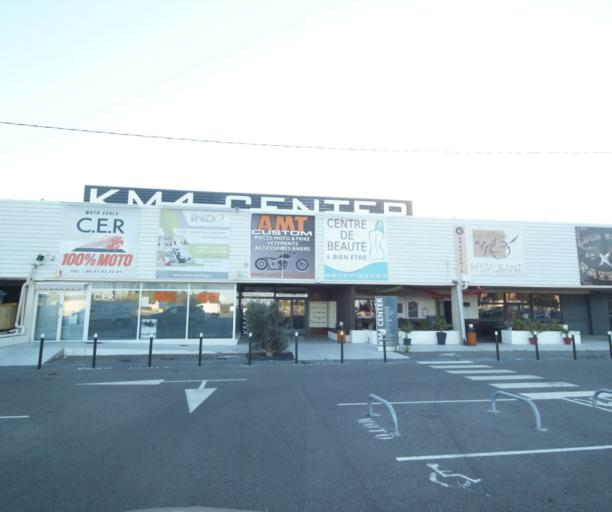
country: FR
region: Languedoc-Roussillon
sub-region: Departement du Gard
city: Caissargues
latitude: 43.8102
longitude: 4.4024
